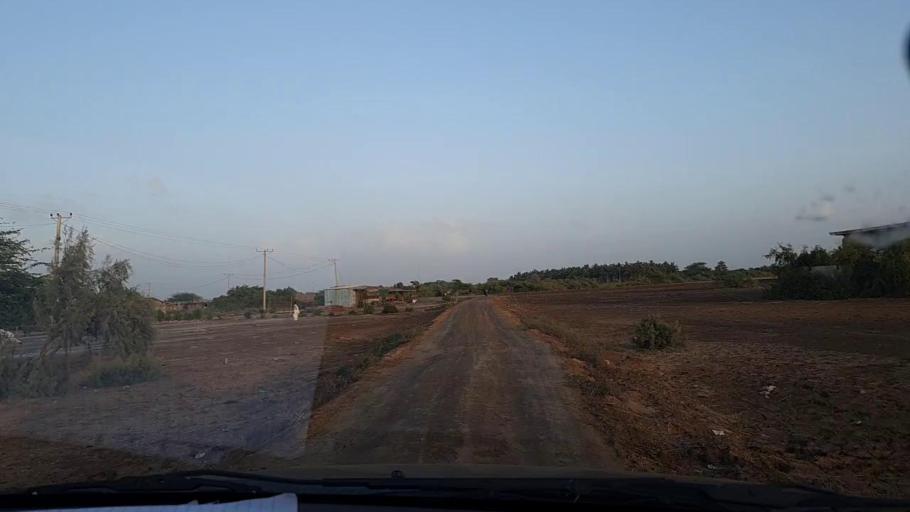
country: PK
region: Sindh
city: Keti Bandar
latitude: 24.1624
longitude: 67.6047
